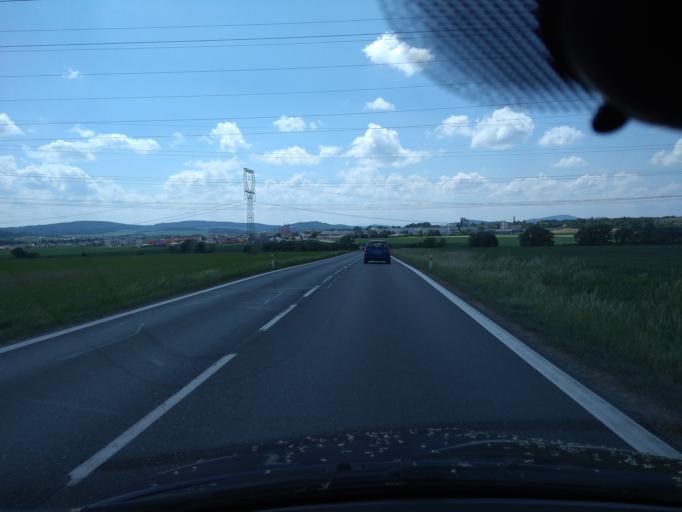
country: CZ
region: Plzensky
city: Prestice
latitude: 49.5912
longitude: 13.3272
